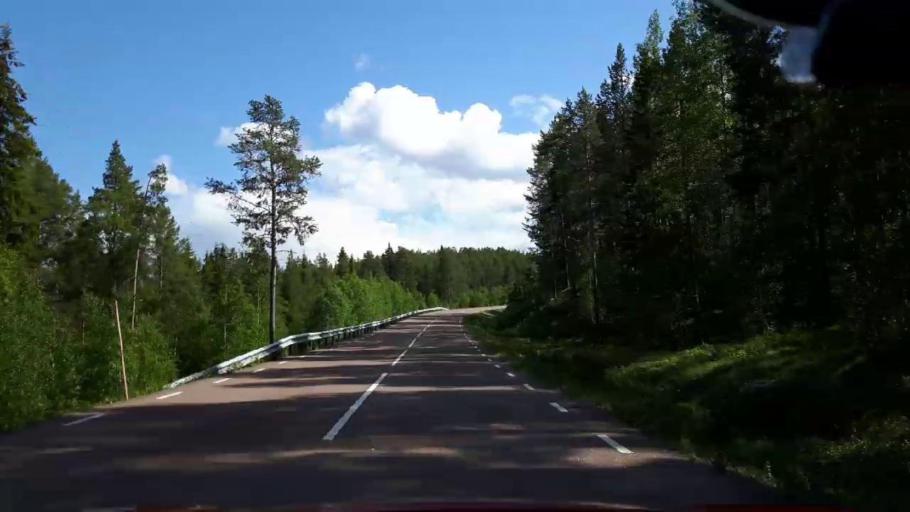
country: SE
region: Jaemtland
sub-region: Krokoms Kommun
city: Valla
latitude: 64.0062
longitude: 14.2391
